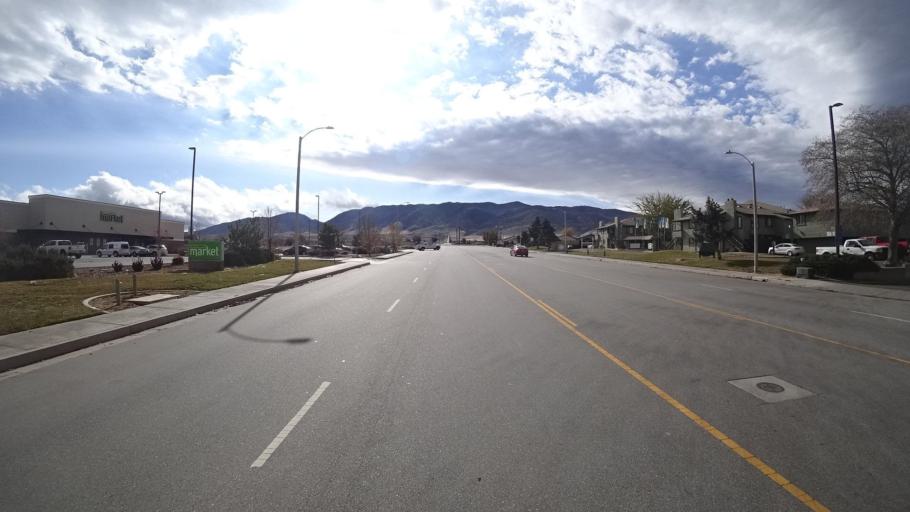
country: US
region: California
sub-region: Kern County
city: Tehachapi
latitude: 35.1223
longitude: -118.4675
